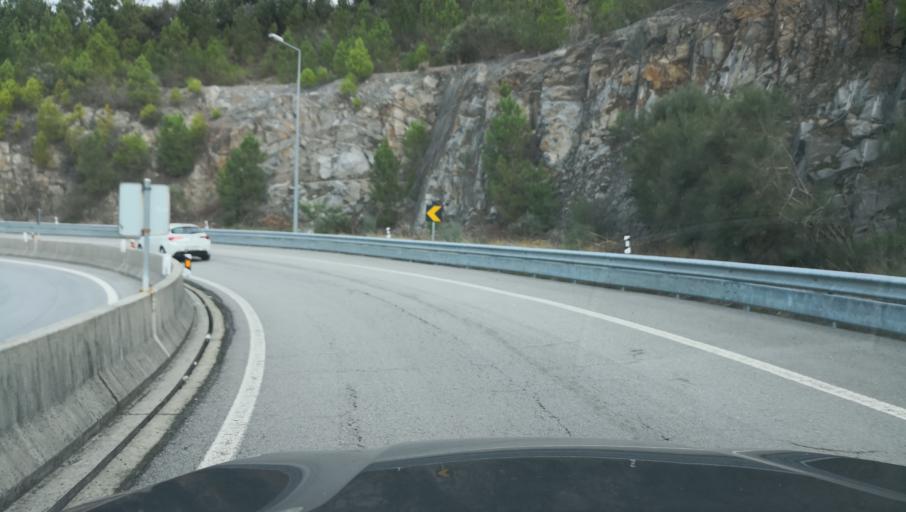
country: PT
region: Vila Real
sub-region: Vila Real
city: Vila Real
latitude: 41.3271
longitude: -7.6982
